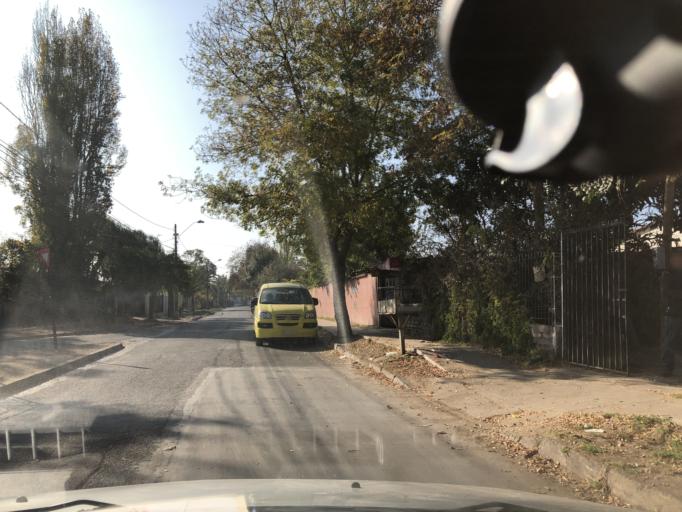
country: CL
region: Santiago Metropolitan
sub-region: Provincia de Cordillera
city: Puente Alto
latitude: -33.6262
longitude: -70.5847
